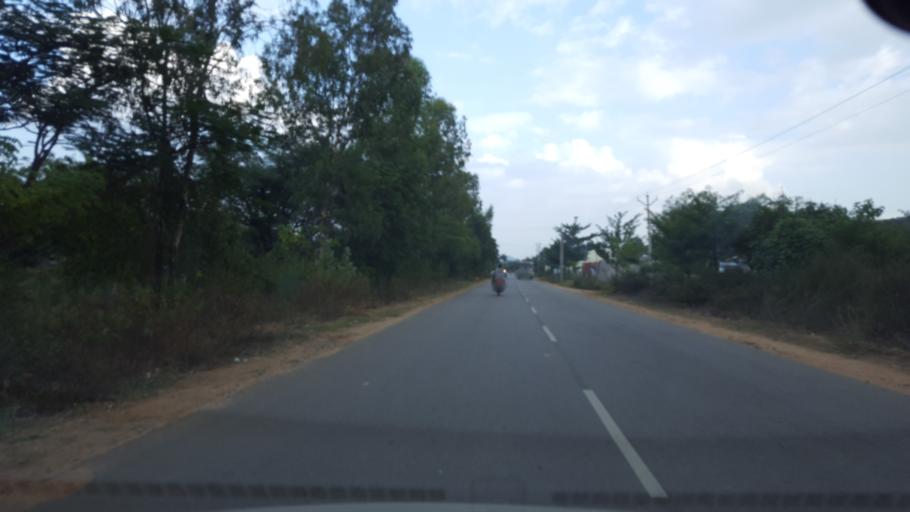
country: IN
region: Telangana
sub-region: Mahbubnagar
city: Mahbubnagar
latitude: 16.7596
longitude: 77.9598
